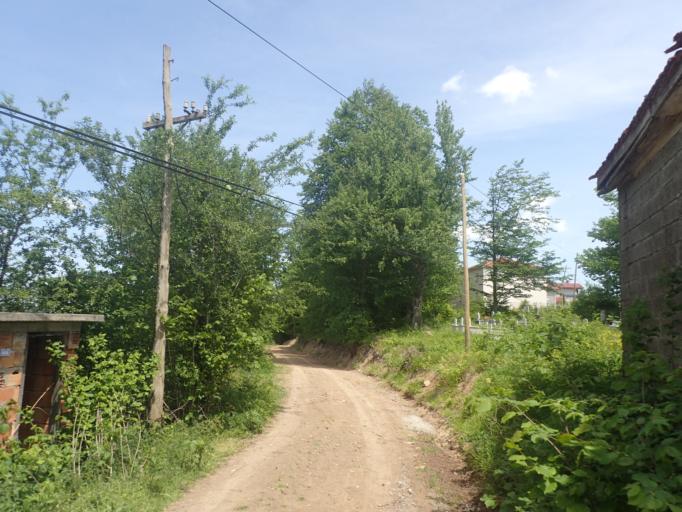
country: TR
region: Ordu
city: Akkus
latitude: 40.8974
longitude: 37.0753
